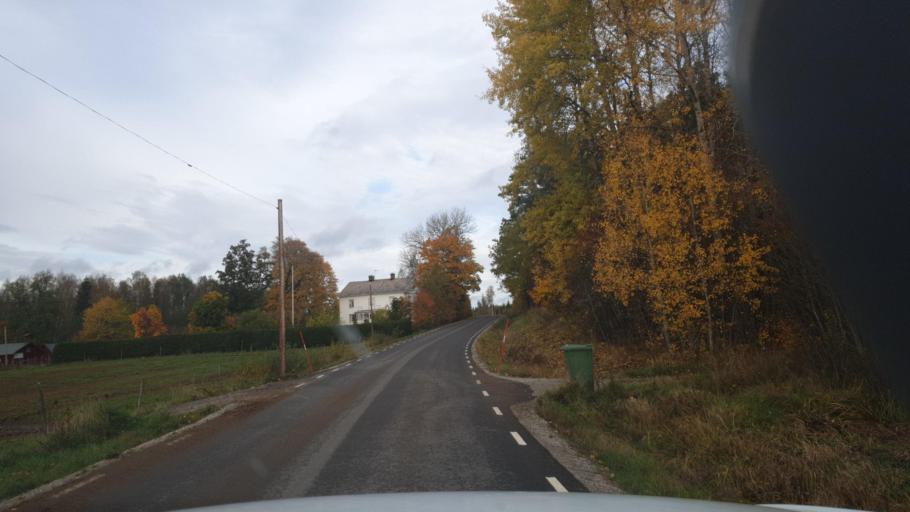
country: SE
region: Vaermland
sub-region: Sunne Kommun
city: Sunne
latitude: 59.6699
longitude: 12.9061
